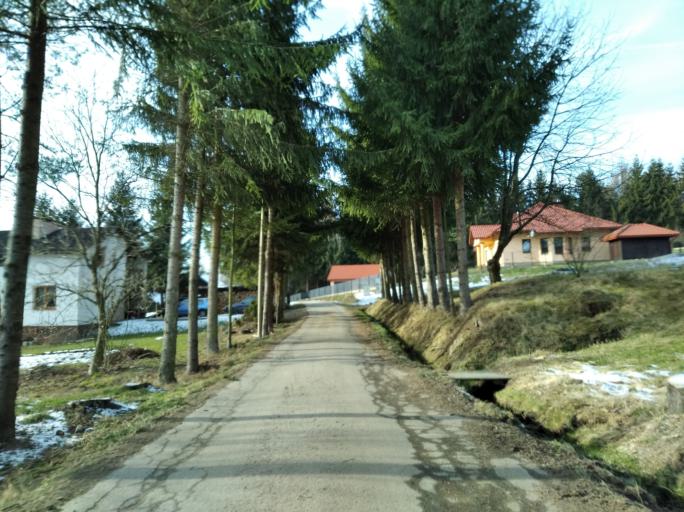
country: PL
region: Subcarpathian Voivodeship
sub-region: Powiat krosnienski
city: Korczyna
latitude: 49.7700
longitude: 21.7943
